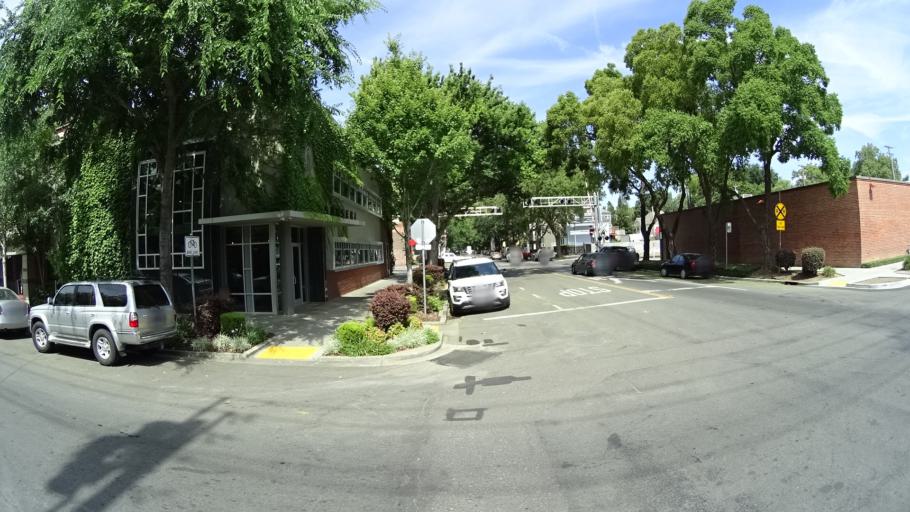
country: US
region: California
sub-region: Sacramento County
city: Sacramento
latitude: 38.5798
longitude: -121.4785
